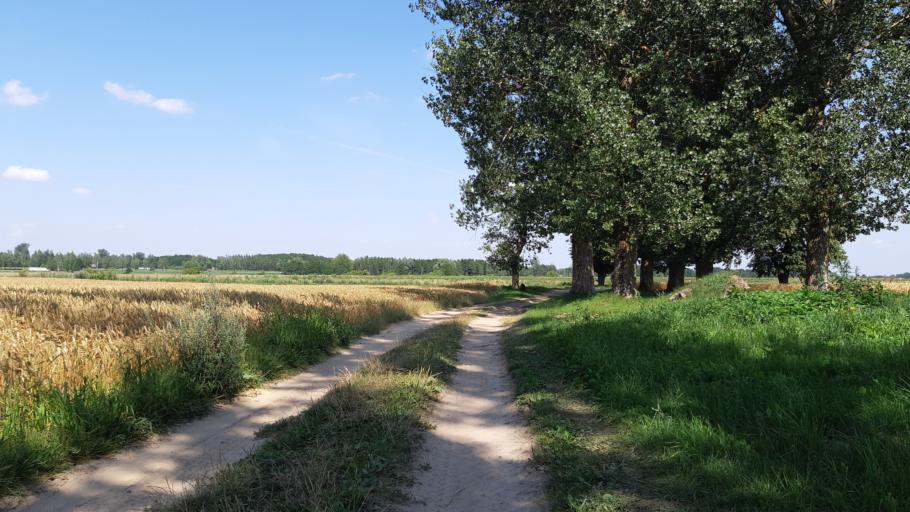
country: LT
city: Virbalis
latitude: 54.6395
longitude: 22.8202
